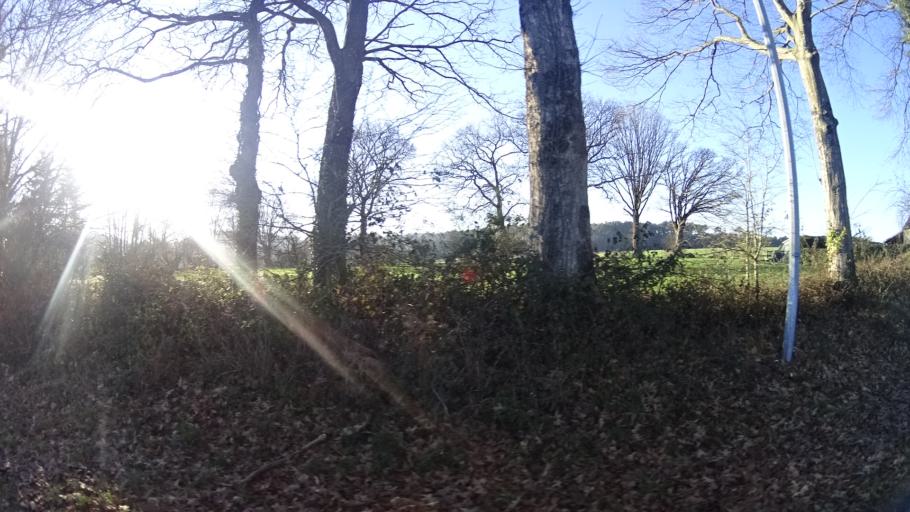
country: FR
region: Brittany
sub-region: Departement du Morbihan
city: Allaire
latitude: 47.6697
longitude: -2.1813
